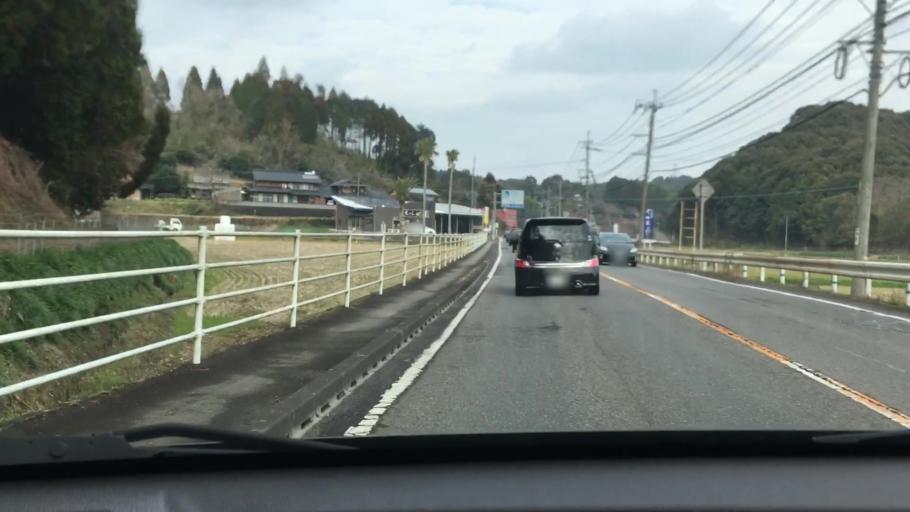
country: JP
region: Saga Prefecture
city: Imaricho-ko
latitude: 33.2982
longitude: 129.9172
